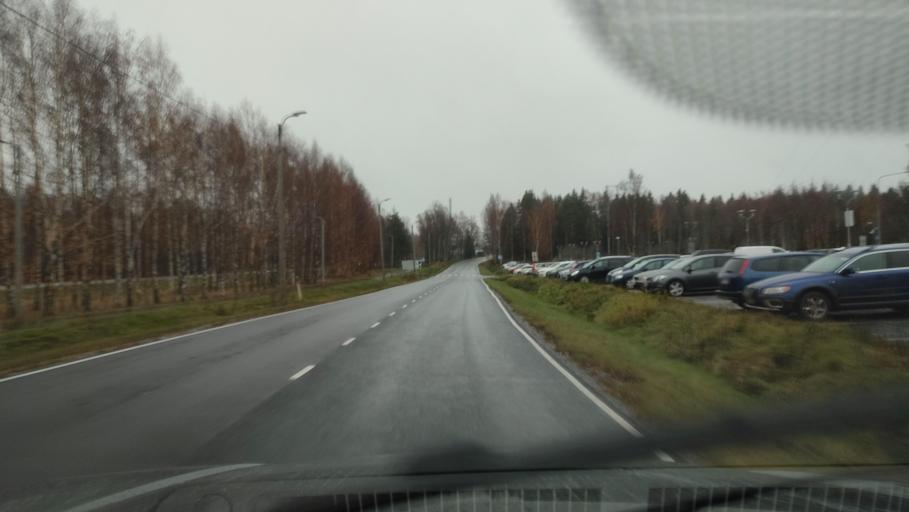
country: FI
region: Ostrobothnia
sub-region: Vaasa
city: Vaasa
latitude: 63.0990
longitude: 21.6476
